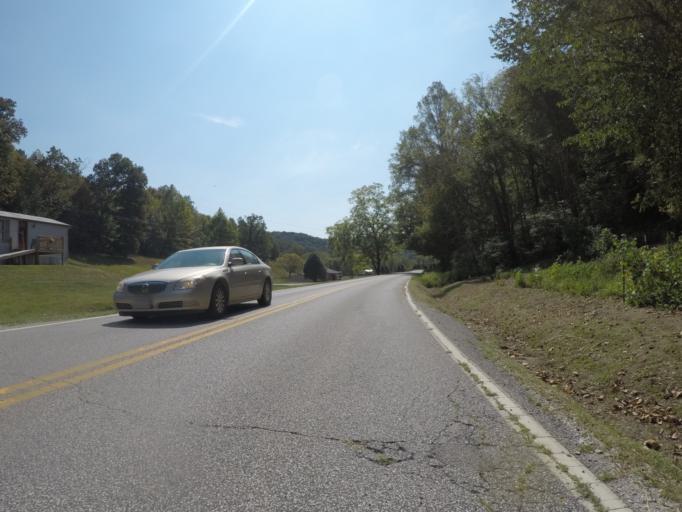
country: US
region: West Virginia
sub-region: Cabell County
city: Lesage
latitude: 38.5271
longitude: -82.3902
